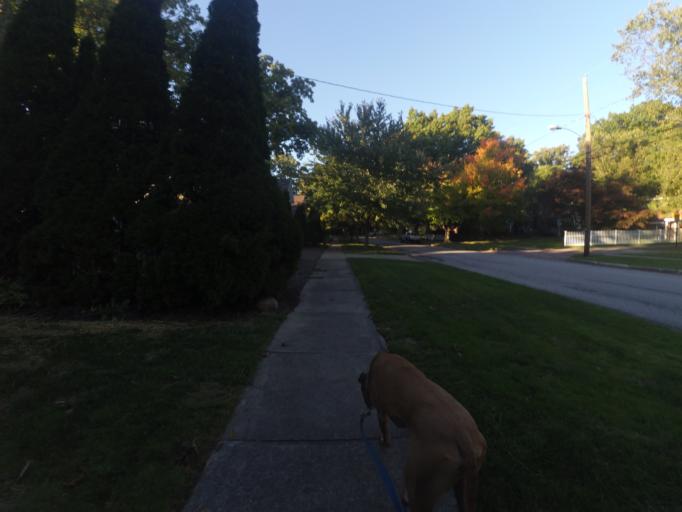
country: US
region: Ohio
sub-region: Portage County
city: Kent
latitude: 41.1543
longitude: -81.3687
